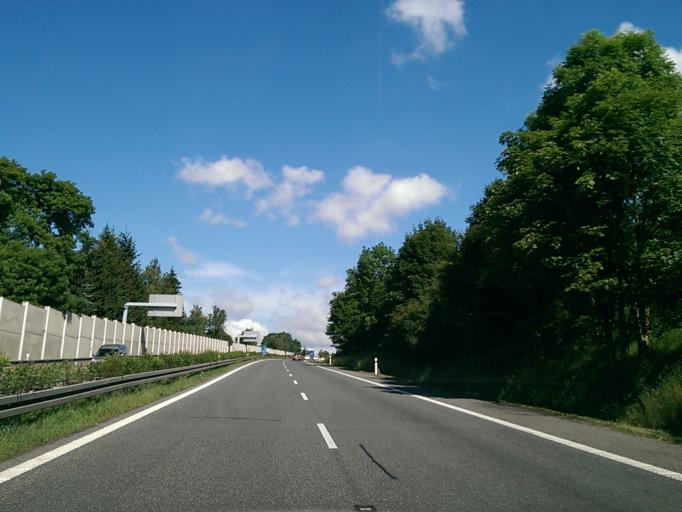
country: CZ
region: Liberecky
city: Hodkovice nad Mohelkou
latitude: 50.6965
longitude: 15.1015
